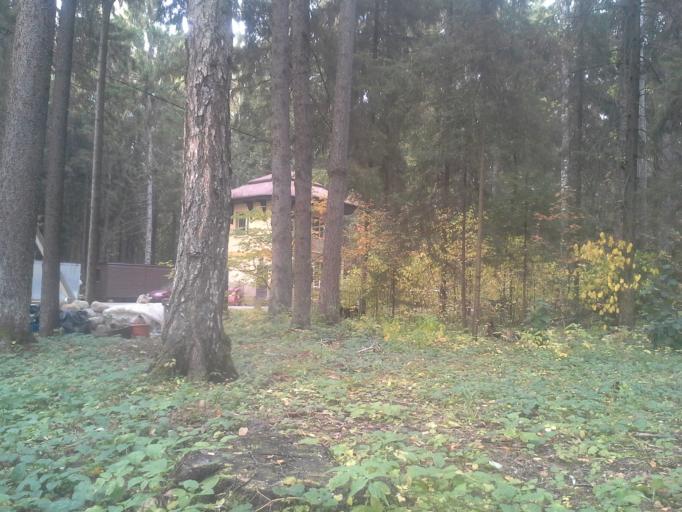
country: RU
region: Moskovskaya
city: Selyatino
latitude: 55.4706
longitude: 36.9703
